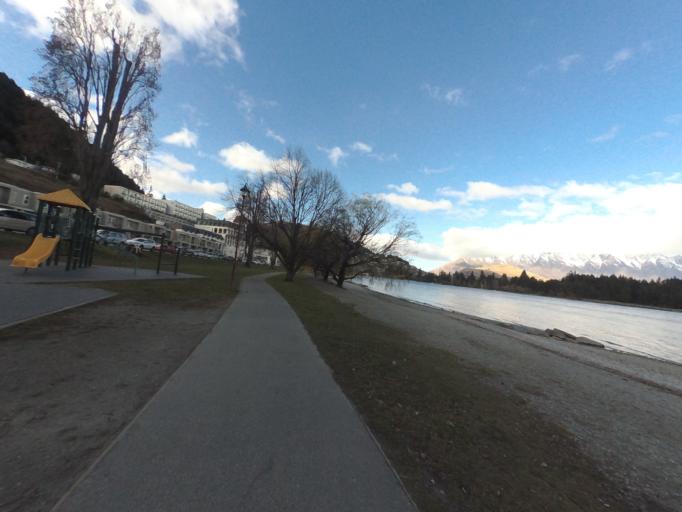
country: NZ
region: Otago
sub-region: Queenstown-Lakes District
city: Queenstown
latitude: -45.0364
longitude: 168.6504
